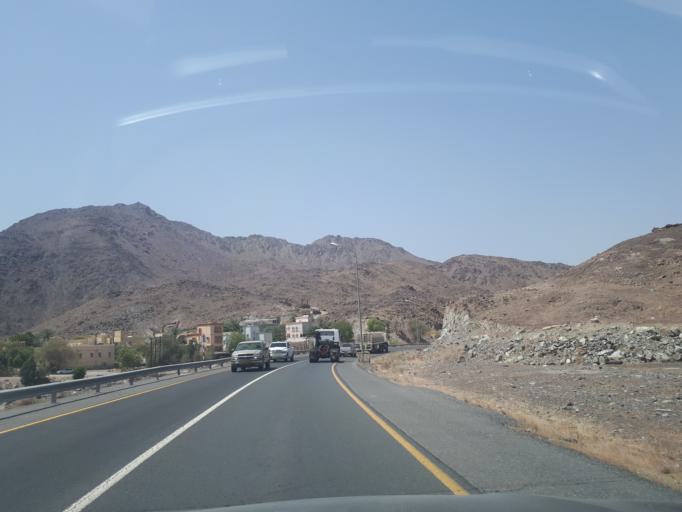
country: OM
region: Muhafazat ad Dakhiliyah
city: Sufalat Sama'il
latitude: 23.2532
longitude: 58.1013
